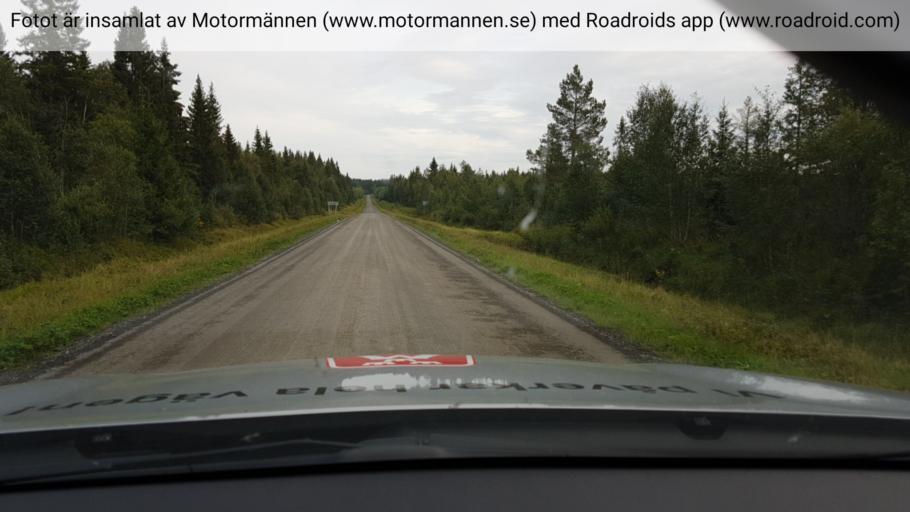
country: SE
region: Jaemtland
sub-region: OEstersunds Kommun
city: Lit
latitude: 63.6525
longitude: 14.9350
